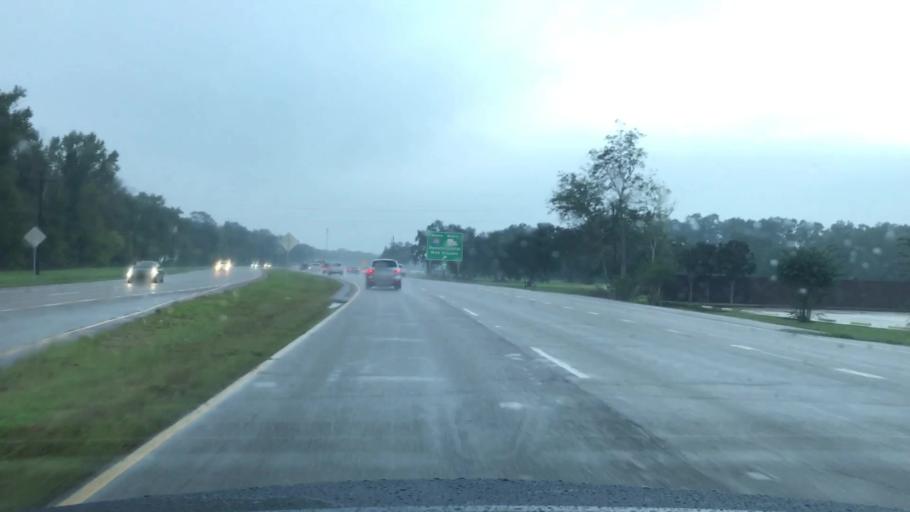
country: US
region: Louisiana
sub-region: Saint Charles Parish
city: Boutte
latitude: 29.8997
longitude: -90.3909
